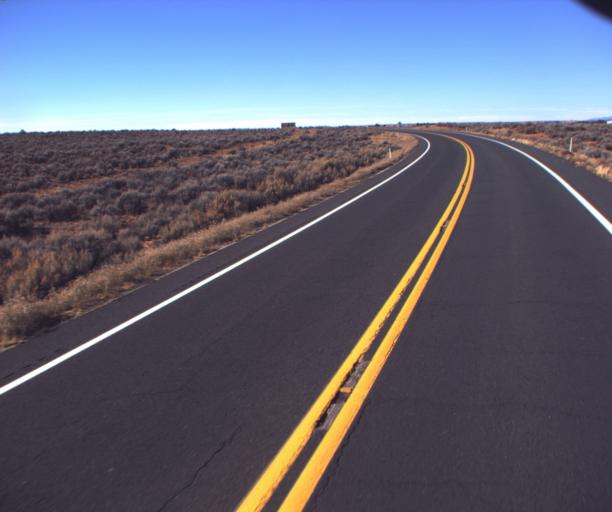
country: US
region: Arizona
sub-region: Coconino County
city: Kaibito
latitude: 36.5498
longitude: -110.7014
